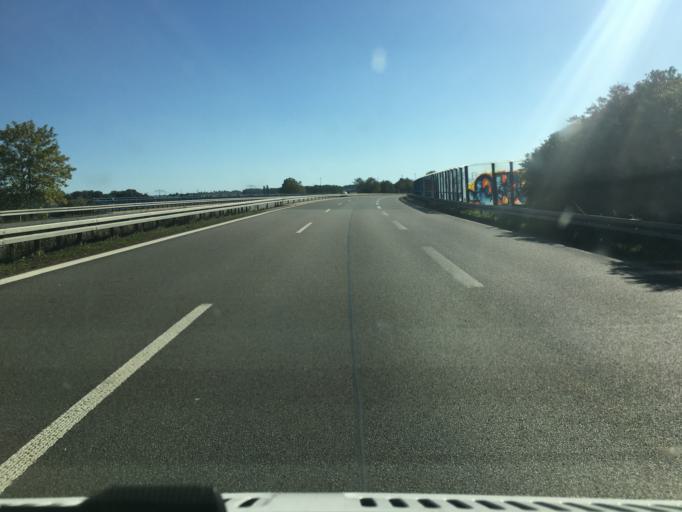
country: DE
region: Saxony
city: Dennheritz
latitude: 50.7842
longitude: 12.4901
